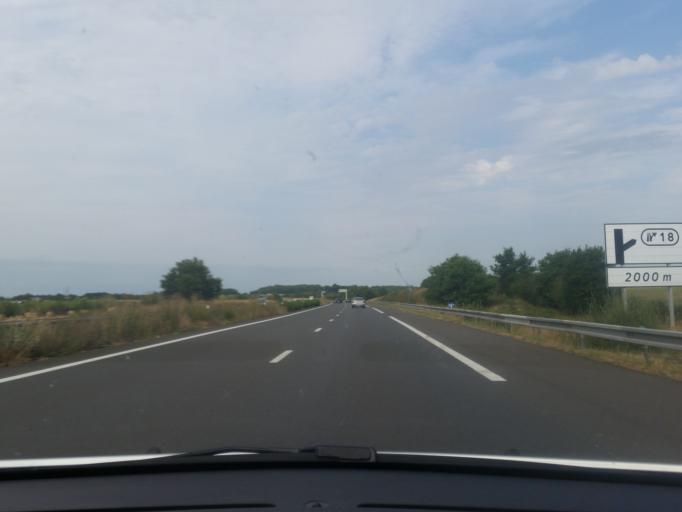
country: FR
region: Pays de la Loire
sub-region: Departement de Maine-et-Loire
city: Saint-Leger-des-Bois
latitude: 47.4498
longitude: -0.7162
